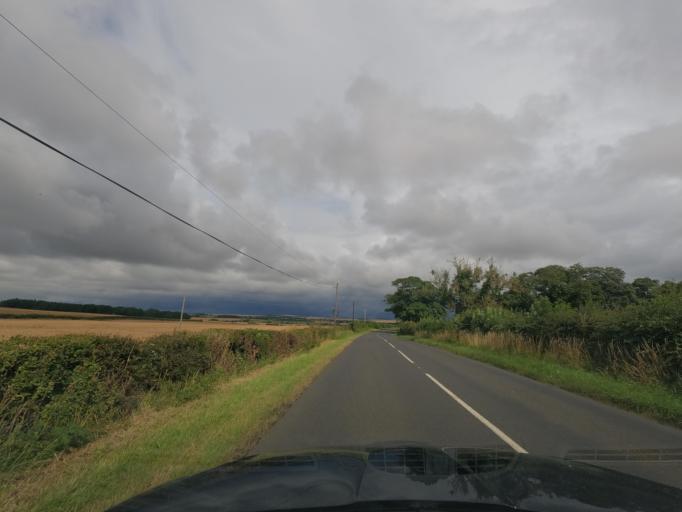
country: GB
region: England
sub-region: Northumberland
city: Ancroft
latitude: 55.6853
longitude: -2.0019
